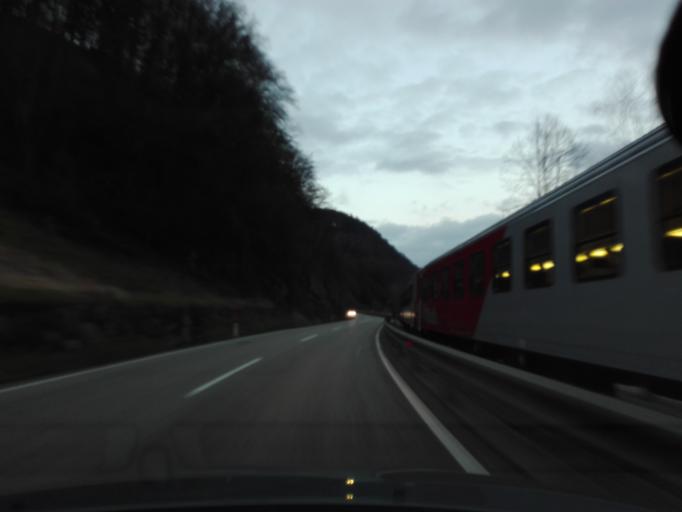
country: AT
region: Upper Austria
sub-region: Politischer Bezirk Perg
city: Bad Kreuzen
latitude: 48.2001
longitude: 14.8451
